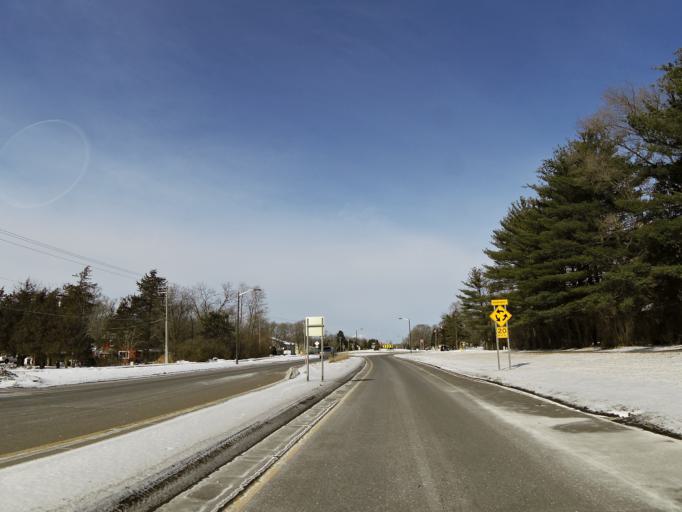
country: US
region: Minnesota
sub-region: Washington County
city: Lakeland
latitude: 44.9483
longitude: -92.7709
